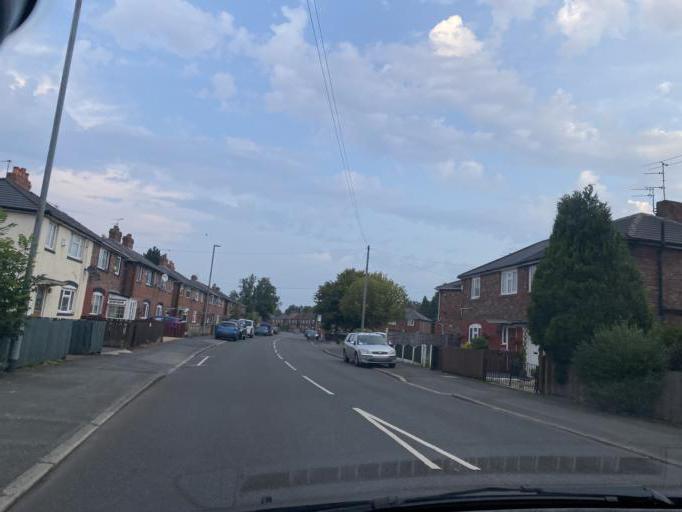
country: GB
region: England
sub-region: Manchester
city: Fallowfield
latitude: 53.4455
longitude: -2.2315
